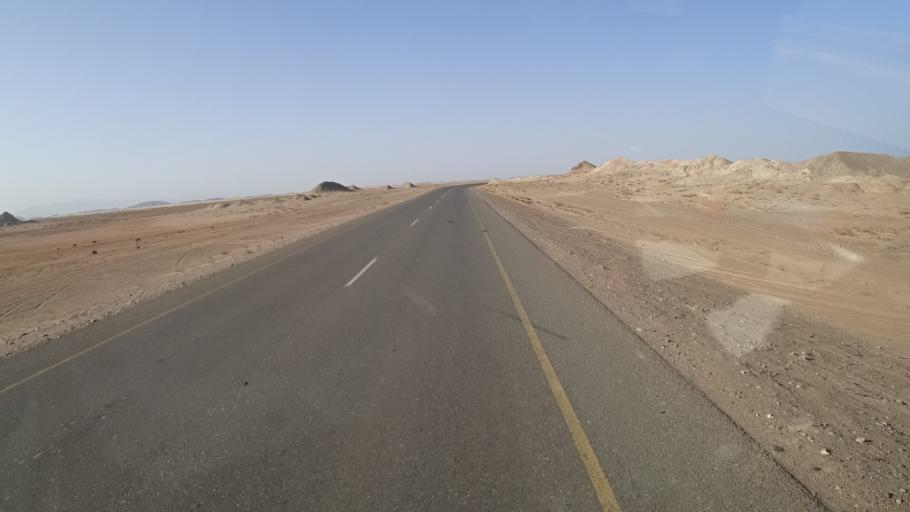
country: OM
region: Ash Sharqiyah
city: Sur
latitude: 22.0560
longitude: 59.6650
